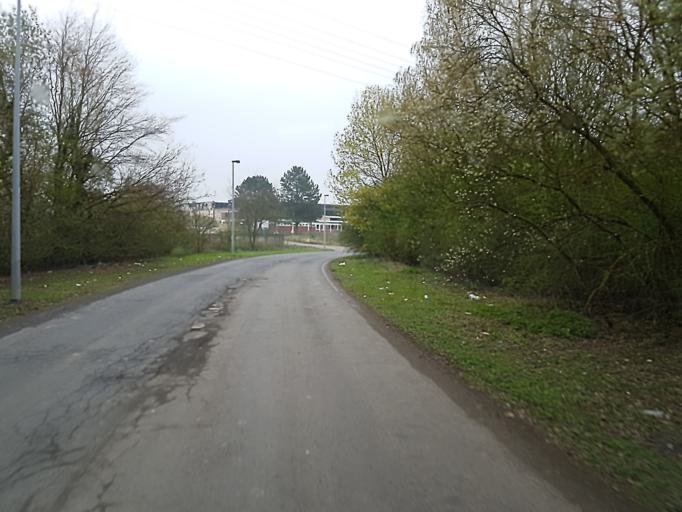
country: BE
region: Wallonia
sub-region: Province du Hainaut
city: Jurbise
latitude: 50.4850
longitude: 3.8926
